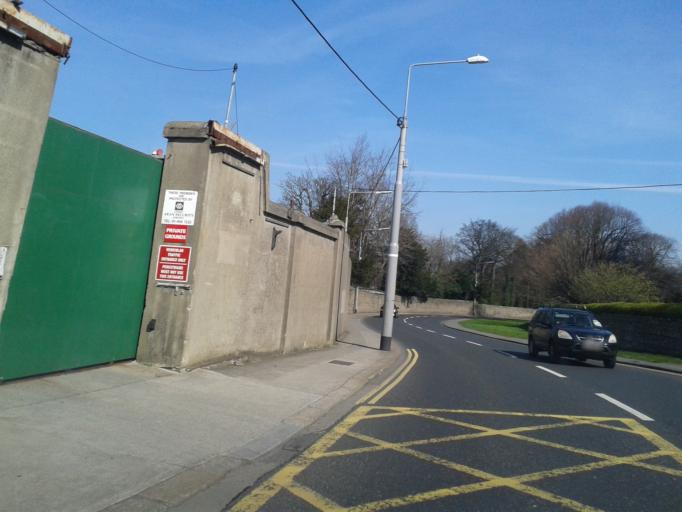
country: IE
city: Milltown
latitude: 53.3165
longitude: -6.2450
